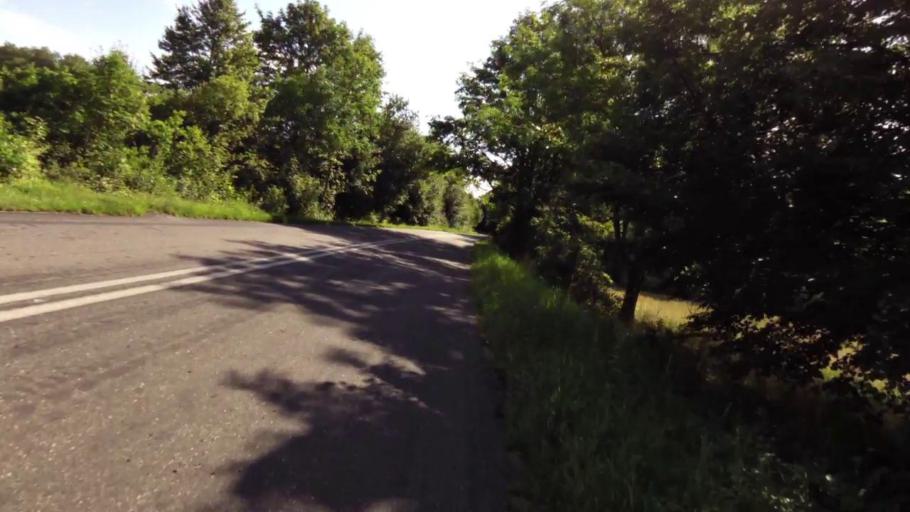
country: PL
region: West Pomeranian Voivodeship
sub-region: Powiat stargardzki
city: Marianowo
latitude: 53.3653
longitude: 15.3314
